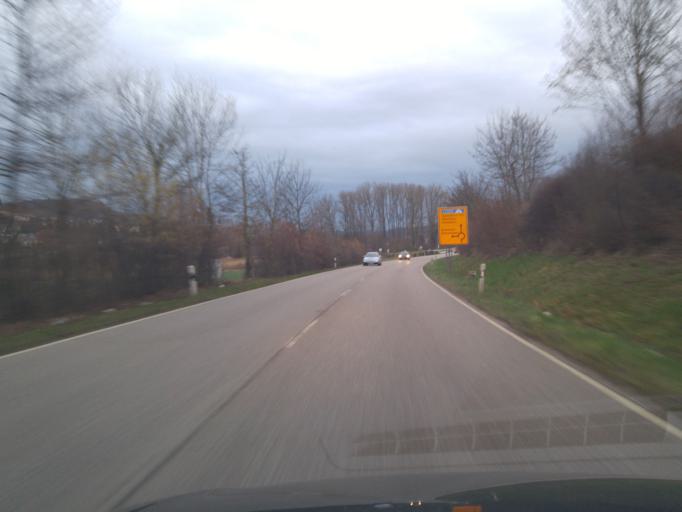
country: DE
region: Baden-Wuerttemberg
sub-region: Regierungsbezirk Stuttgart
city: Erlenbach
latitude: 49.1781
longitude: 9.2473
